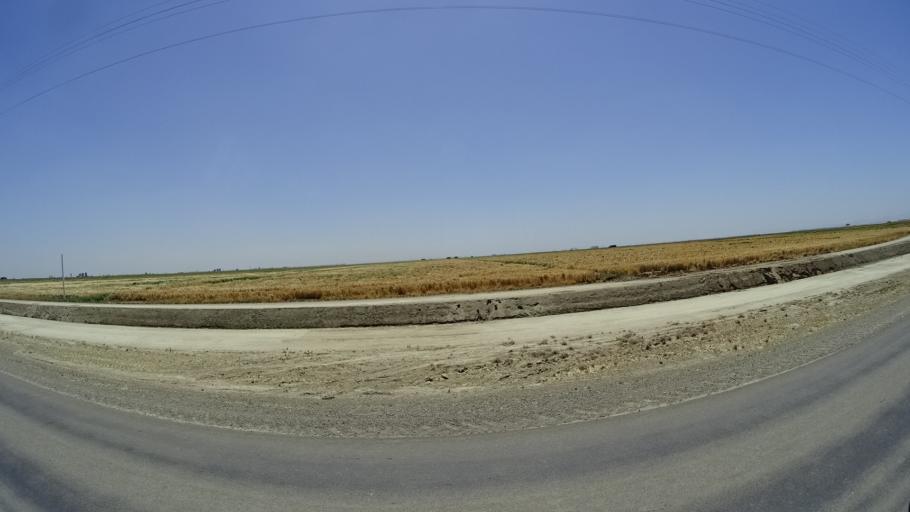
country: US
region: California
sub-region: Kings County
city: Home Garden
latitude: 36.1966
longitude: -119.6225
